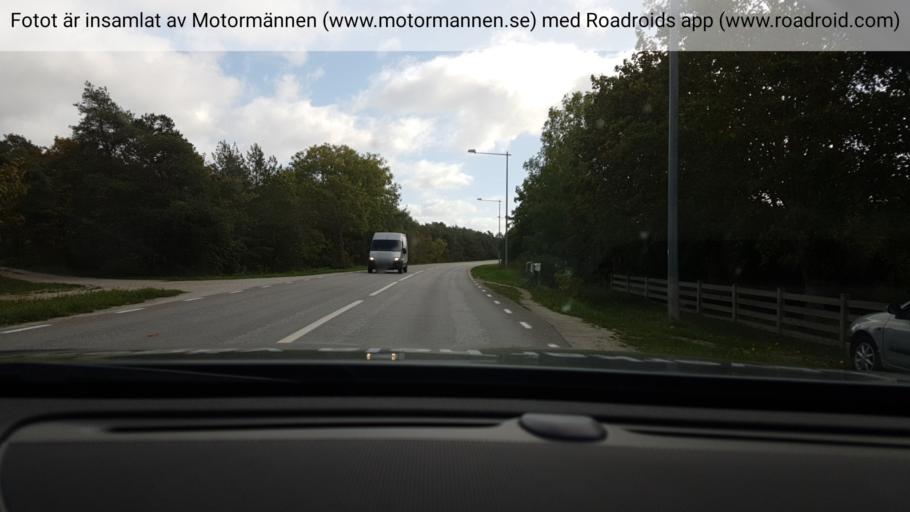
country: SE
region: Gotland
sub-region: Gotland
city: Slite
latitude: 57.8566
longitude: 19.0134
